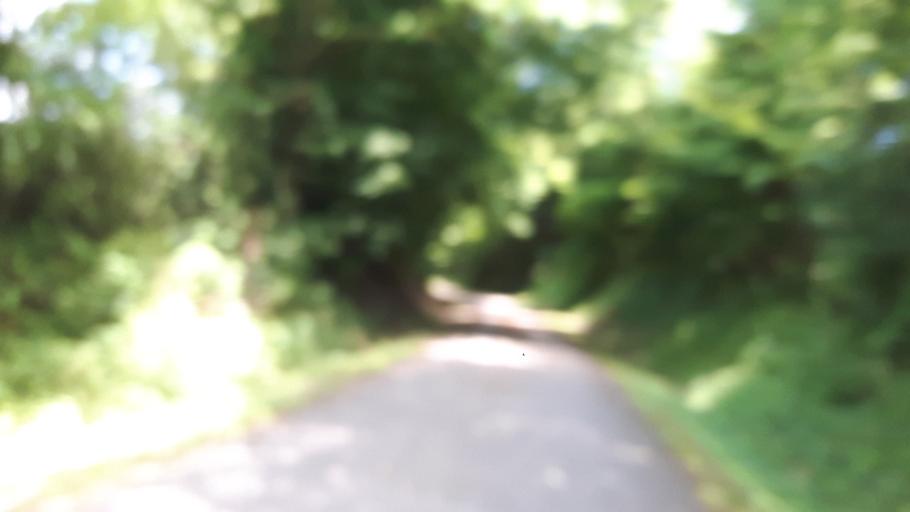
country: DE
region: Baden-Wuerttemberg
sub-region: Regierungsbezirk Stuttgart
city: Jagsthausen
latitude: 49.2479
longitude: 9.4428
